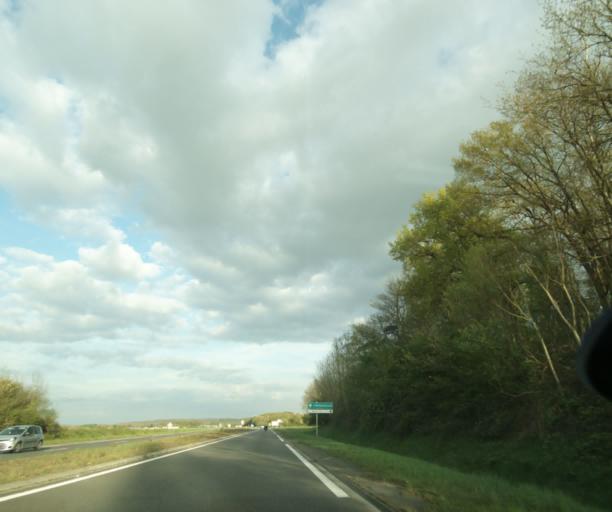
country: FR
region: Ile-de-France
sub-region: Departement de Seine-et-Marne
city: Barbizon
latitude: 48.4578
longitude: 2.5857
